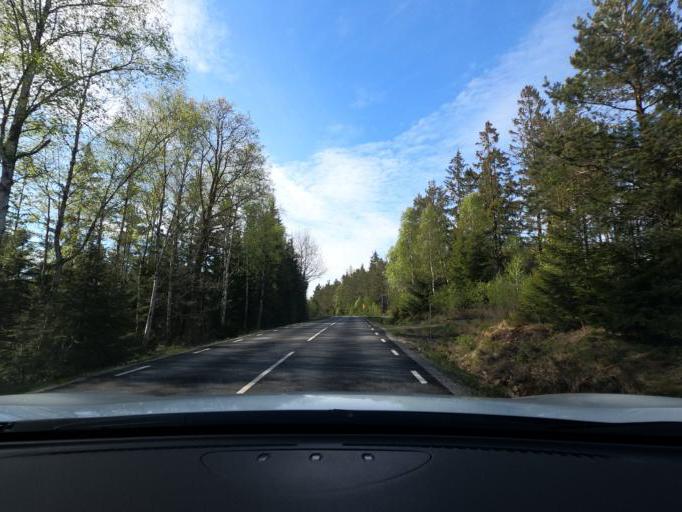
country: SE
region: Vaestra Goetaland
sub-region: Harryda Kommun
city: Landvetter
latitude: 57.6376
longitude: 12.2584
